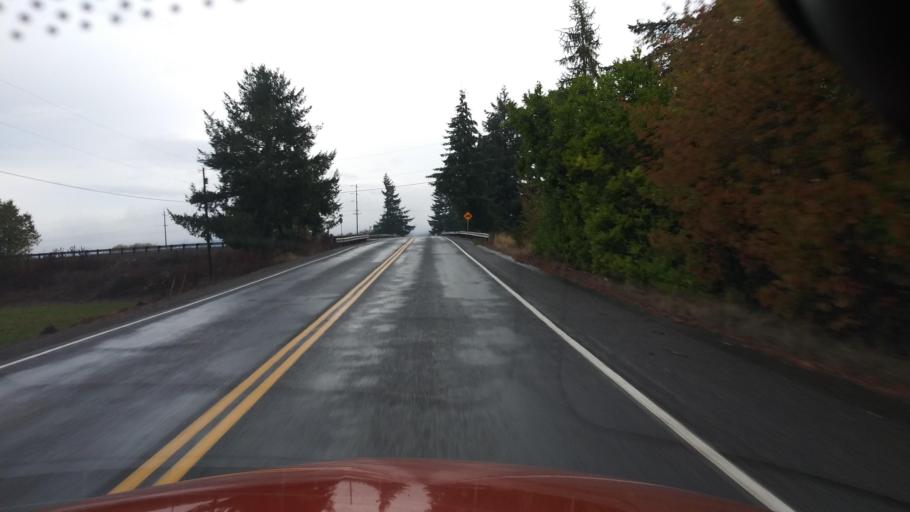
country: US
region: Oregon
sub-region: Washington County
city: North Plains
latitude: 45.5952
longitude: -123.0145
